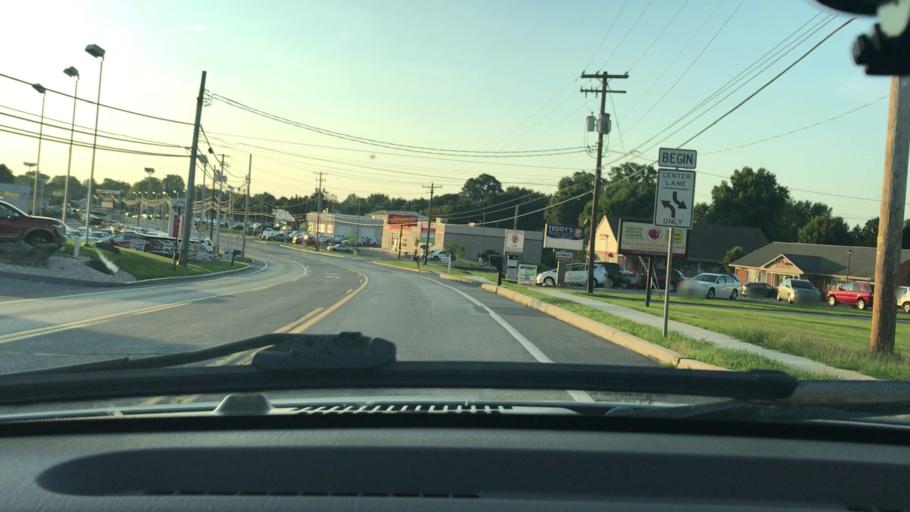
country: US
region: Pennsylvania
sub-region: Lancaster County
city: East Petersburg
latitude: 40.0905
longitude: -76.3466
